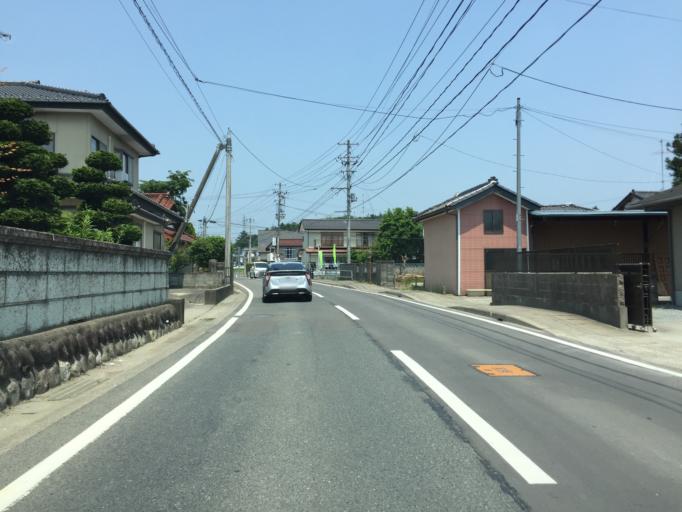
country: JP
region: Miyagi
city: Marumori
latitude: 37.8140
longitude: 140.8990
